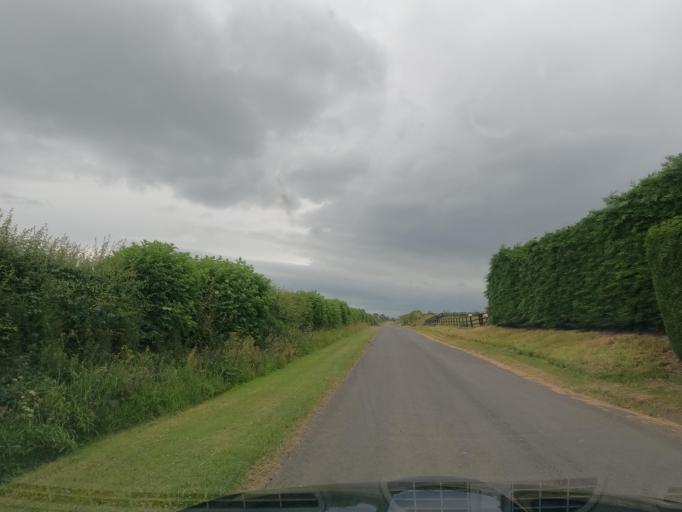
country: GB
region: England
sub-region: Northumberland
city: Ancroft
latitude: 55.6692
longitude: -2.0204
